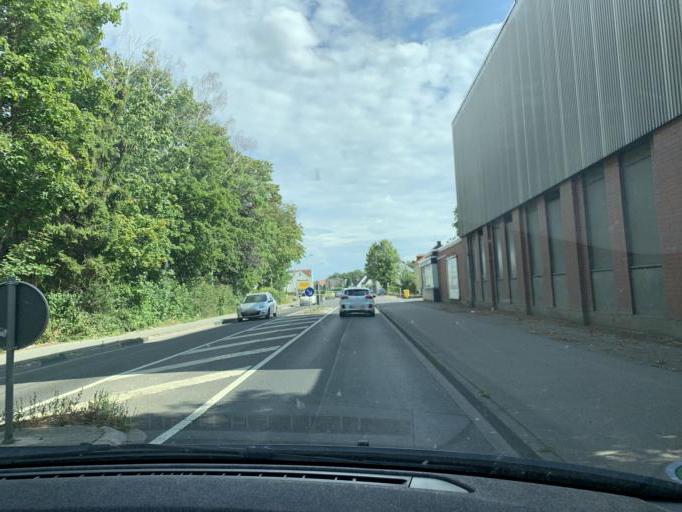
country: DE
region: North Rhine-Westphalia
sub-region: Regierungsbezirk Koln
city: Niederzier
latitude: 50.8554
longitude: 6.4400
